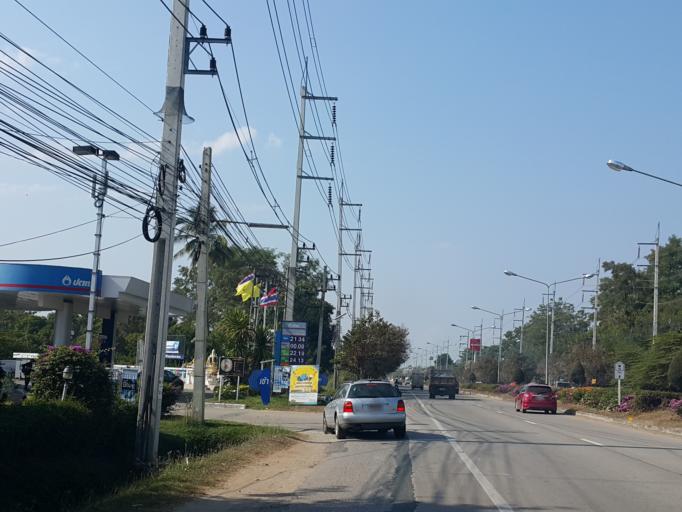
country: TH
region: Chiang Mai
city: San Sai
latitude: 18.8468
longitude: 99.0796
